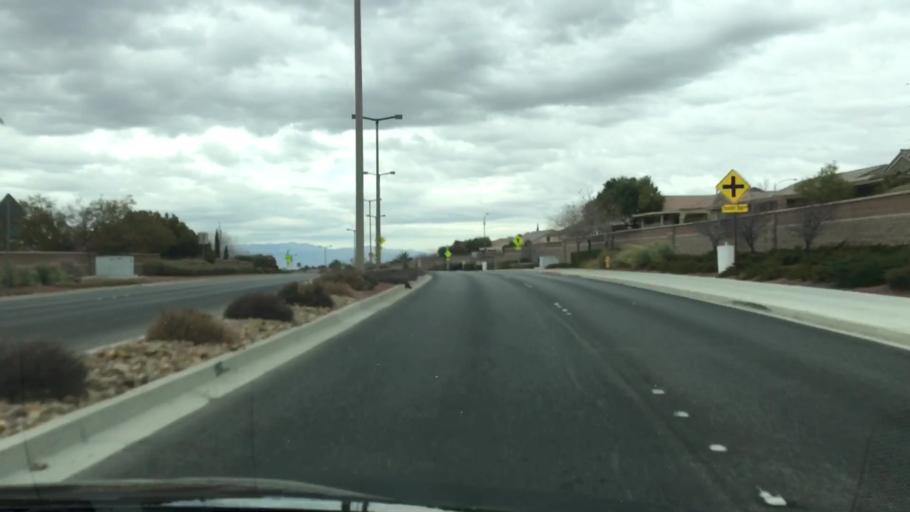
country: US
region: Nevada
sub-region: Clark County
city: Whitney
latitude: 35.9517
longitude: -115.1145
